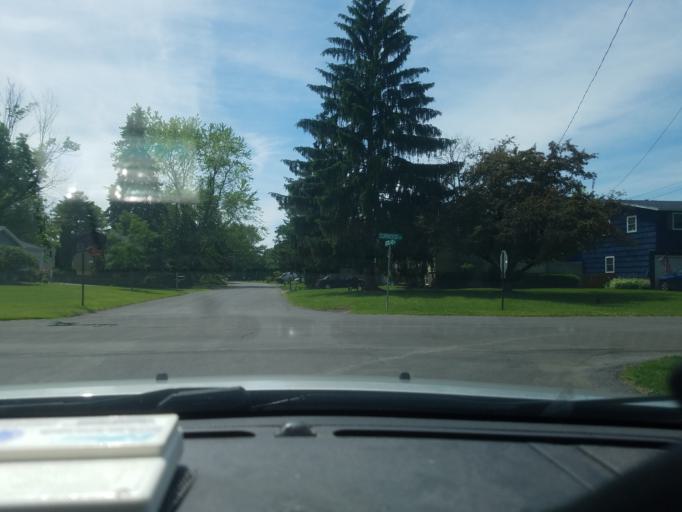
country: US
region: New York
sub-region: Onondaga County
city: East Syracuse
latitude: 43.0815
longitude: -76.0652
